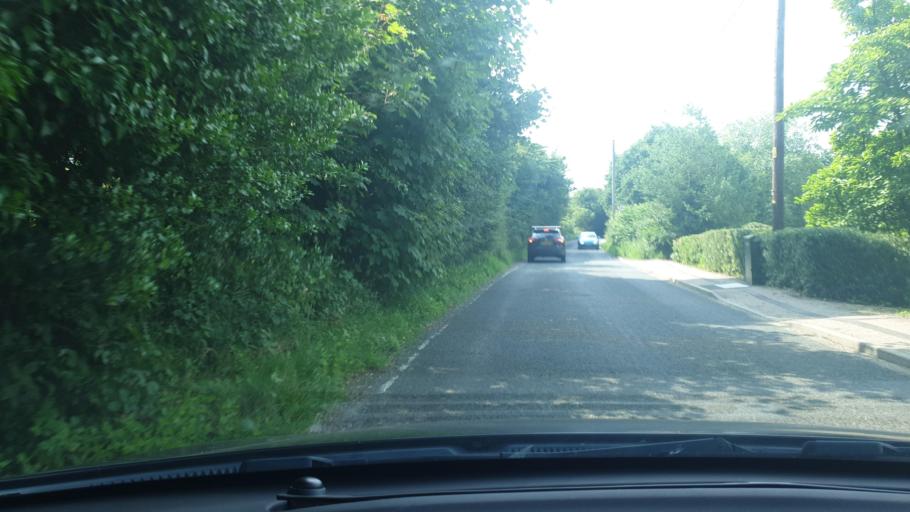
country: GB
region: England
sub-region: Suffolk
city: East Bergholt
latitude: 51.9579
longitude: 0.9791
